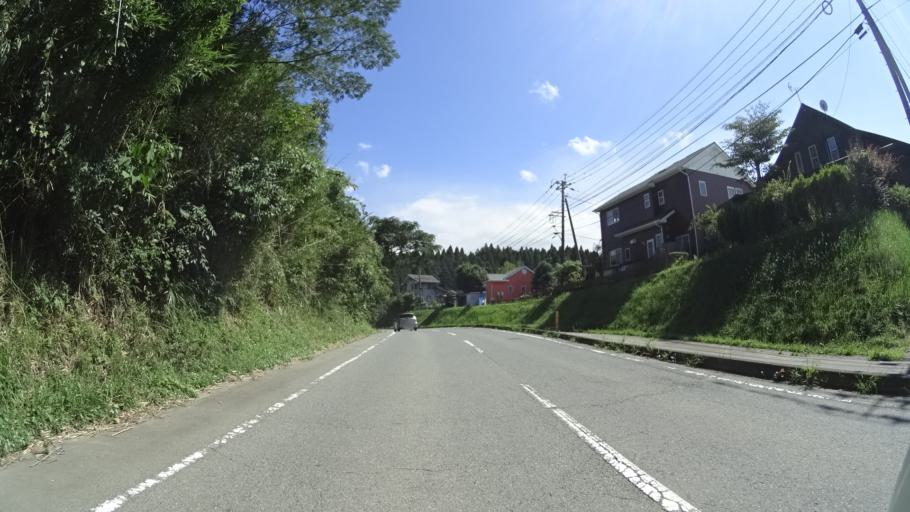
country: JP
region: Kumamoto
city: Aso
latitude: 32.8819
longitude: 131.0026
